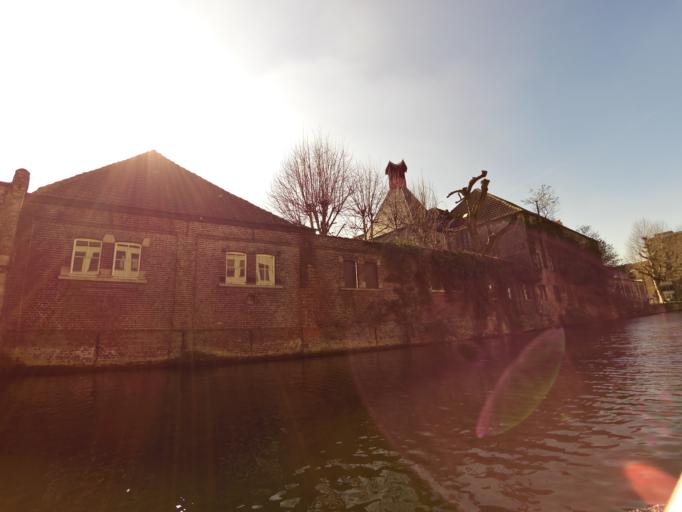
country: BE
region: Flanders
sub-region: Provincie Oost-Vlaanderen
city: Gent
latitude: 51.0597
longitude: 3.7164
